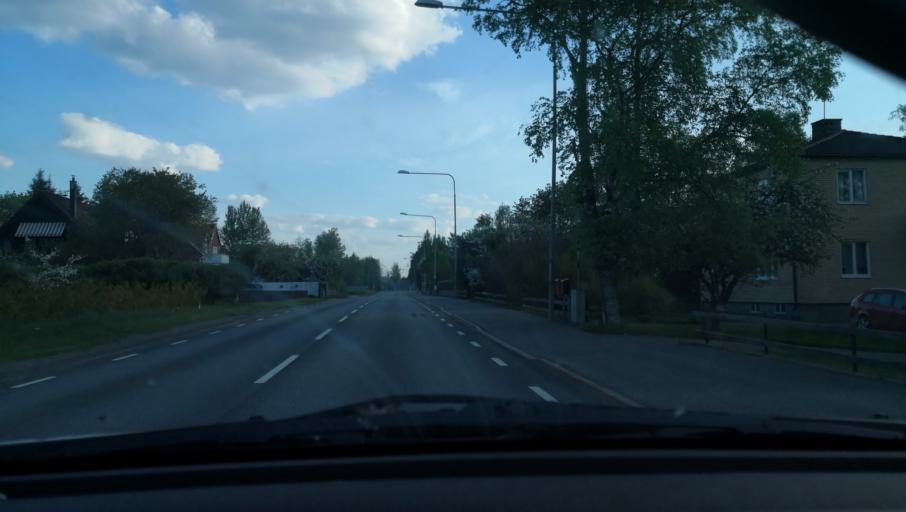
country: SE
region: Joenkoeping
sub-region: Nassjo Kommun
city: Bodafors
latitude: 57.5609
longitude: 14.6966
